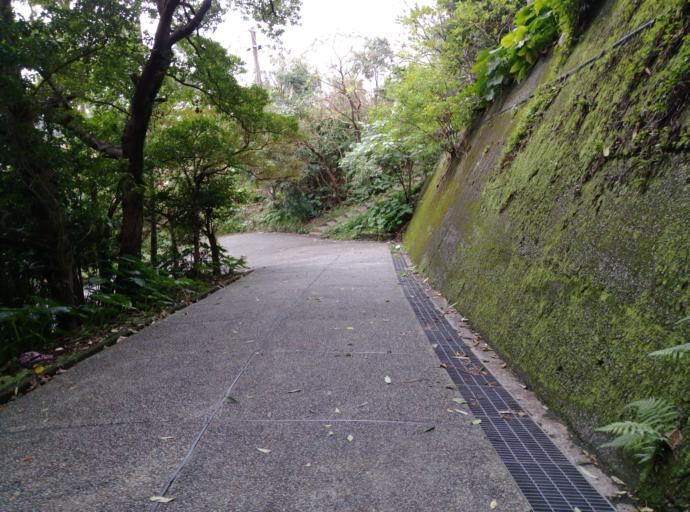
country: TW
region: Taiwan
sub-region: Keelung
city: Keelung
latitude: 25.1318
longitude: 121.7477
